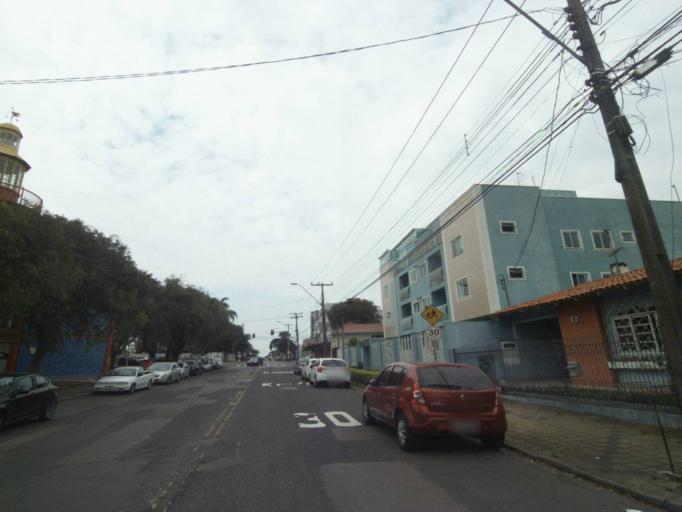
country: BR
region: Parana
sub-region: Curitiba
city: Curitiba
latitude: -25.4624
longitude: -49.3054
